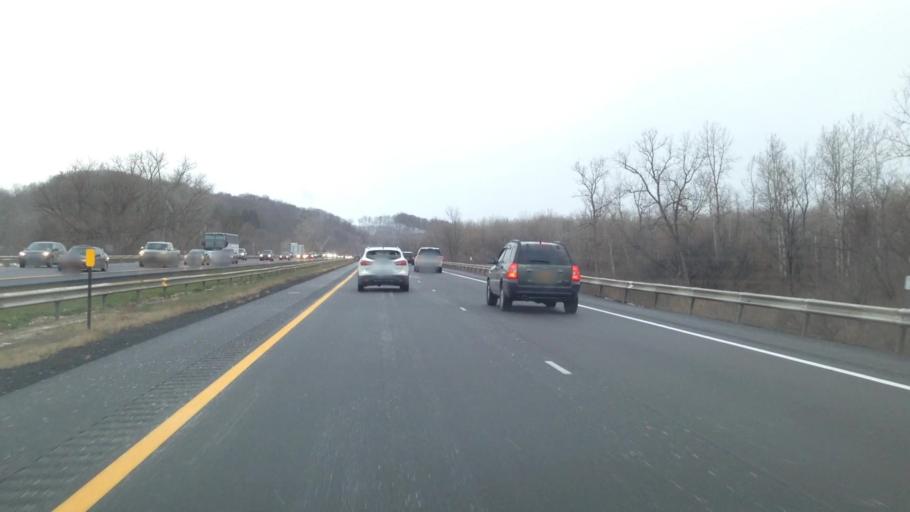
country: US
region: New York
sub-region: Montgomery County
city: Canajoharie
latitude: 42.9087
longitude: -74.5912
